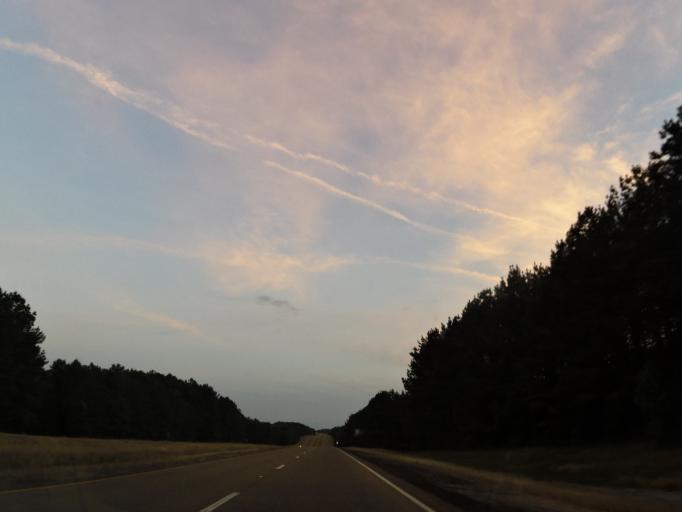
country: US
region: Mississippi
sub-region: Lauderdale County
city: Meridian Station
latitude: 32.6332
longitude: -88.4973
